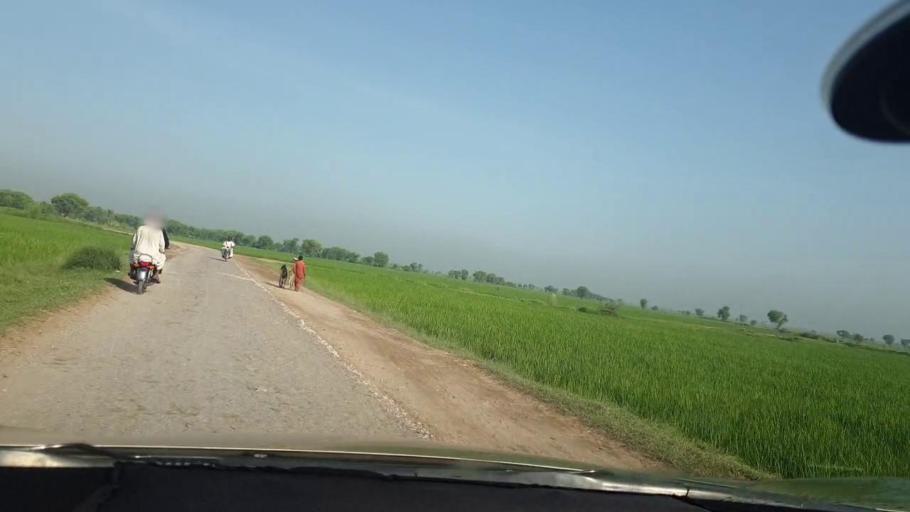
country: PK
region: Sindh
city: Kambar
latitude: 27.6580
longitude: 68.0260
